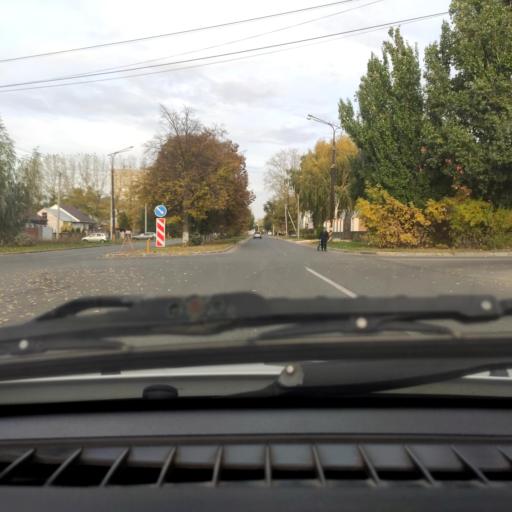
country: RU
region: Samara
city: Tol'yatti
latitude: 53.5162
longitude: 49.4000
